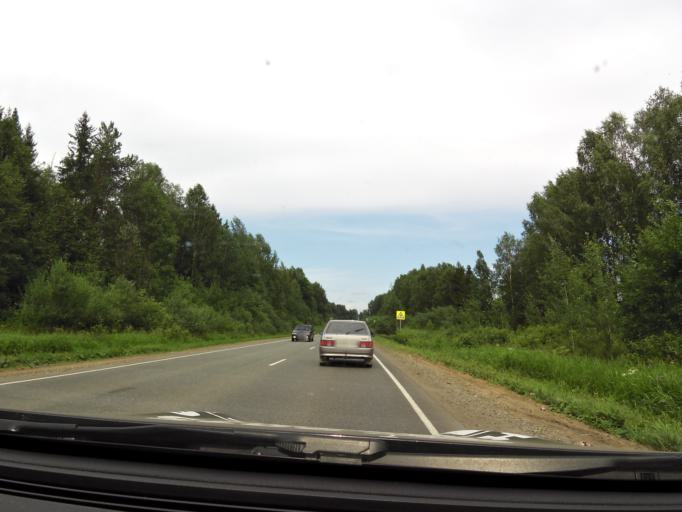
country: RU
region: Kirov
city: Vakhrushi
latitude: 58.6446
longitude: 49.8573
